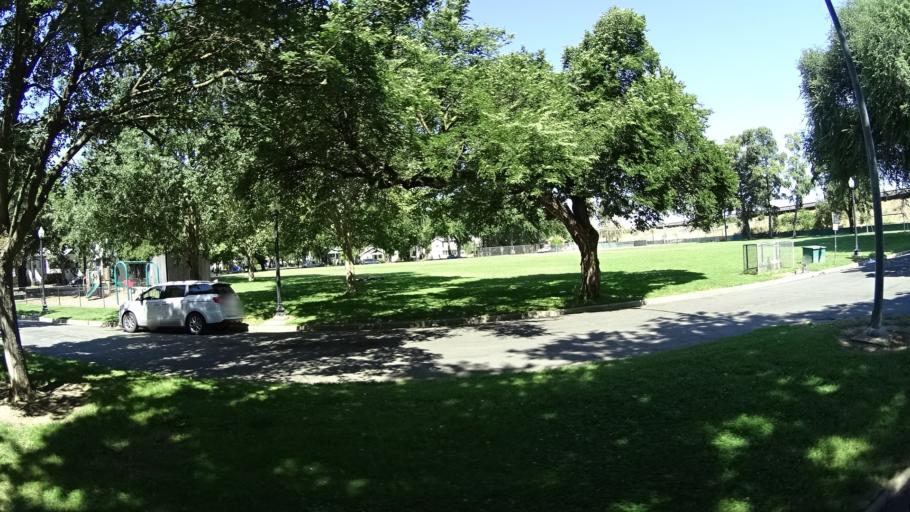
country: US
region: California
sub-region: Sacramento County
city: Sacramento
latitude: 38.5841
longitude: -121.4736
